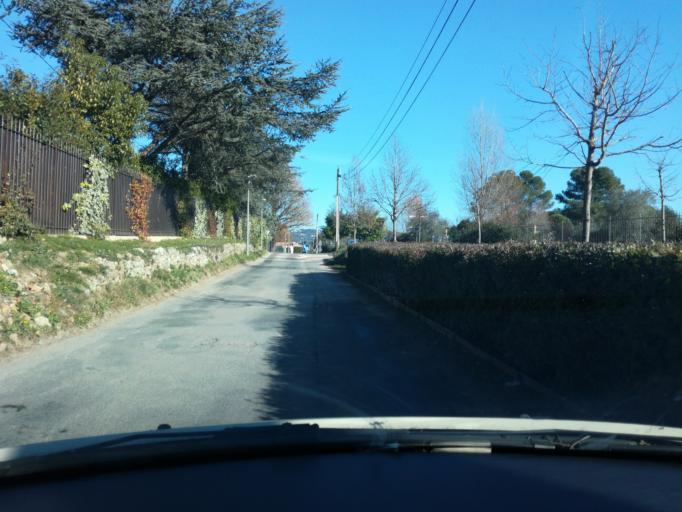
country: FR
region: Provence-Alpes-Cote d'Azur
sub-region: Departement des Alpes-Maritimes
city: La Roquette-sur-Siagne
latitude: 43.6010
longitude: 6.9498
